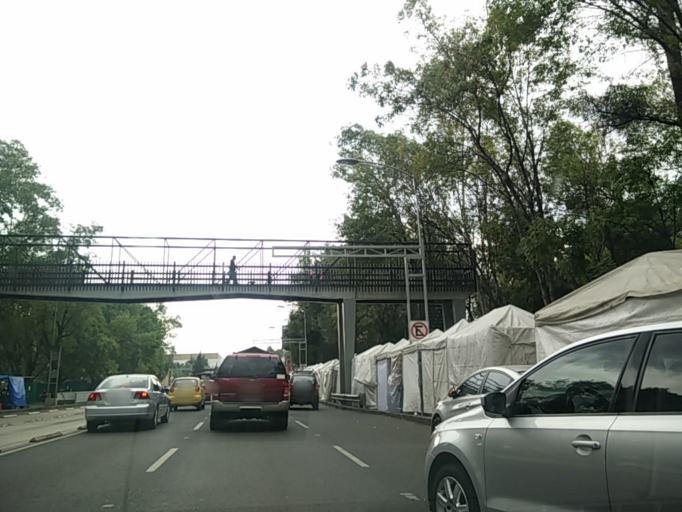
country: MX
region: Mexico City
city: Benito Juarez
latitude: 19.4089
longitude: -99.1551
